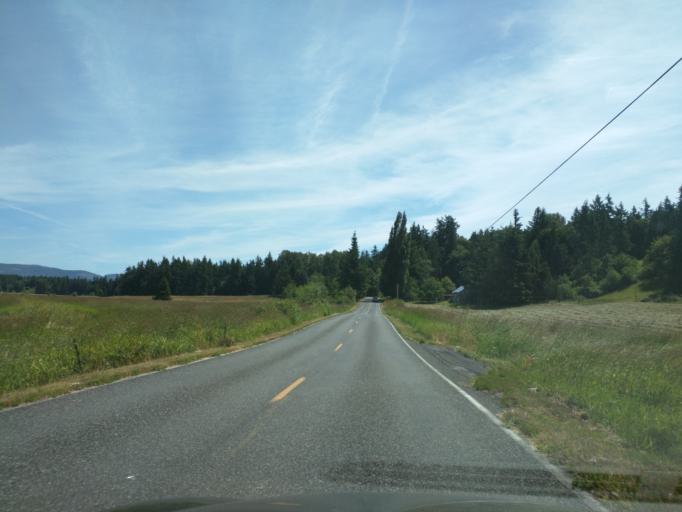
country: US
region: Washington
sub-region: Whatcom County
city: Geneva
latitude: 48.8040
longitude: -122.4140
